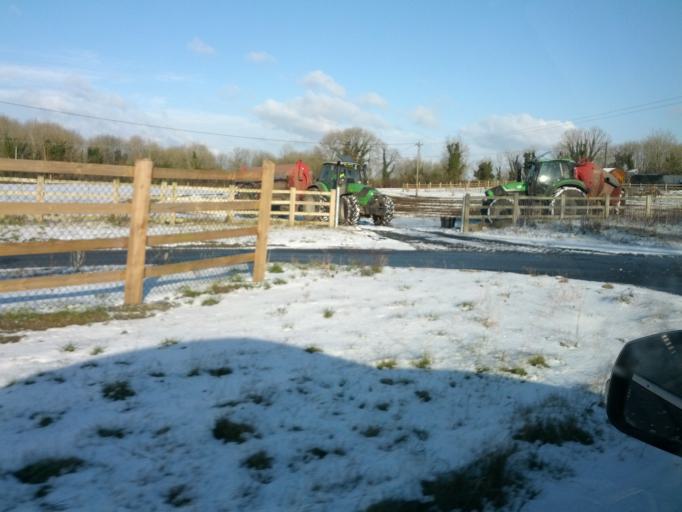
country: IE
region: Connaught
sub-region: County Galway
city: Gort
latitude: 53.1865
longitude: -8.8307
